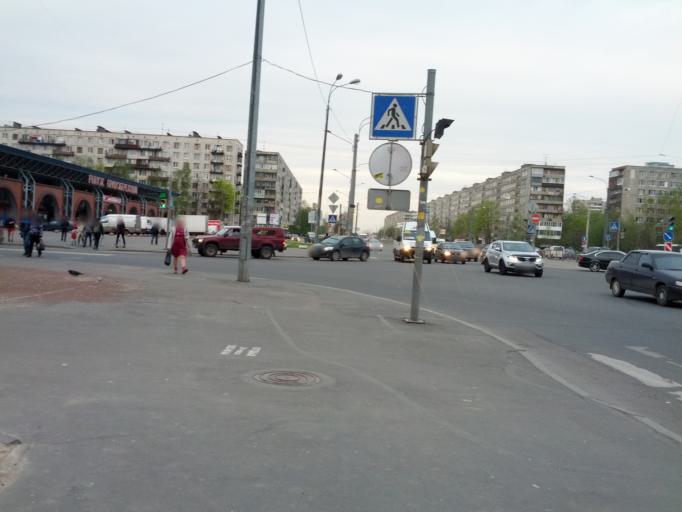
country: RU
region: St.-Petersburg
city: Obukhovo
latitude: 59.9035
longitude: 30.4683
